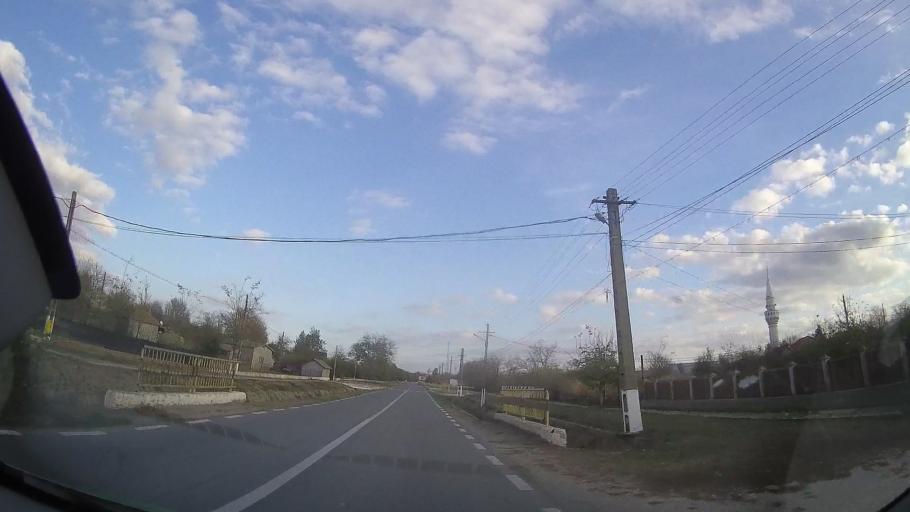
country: RO
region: Constanta
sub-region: Comuna Independenta
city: Independenta
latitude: 43.9536
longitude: 28.0778
